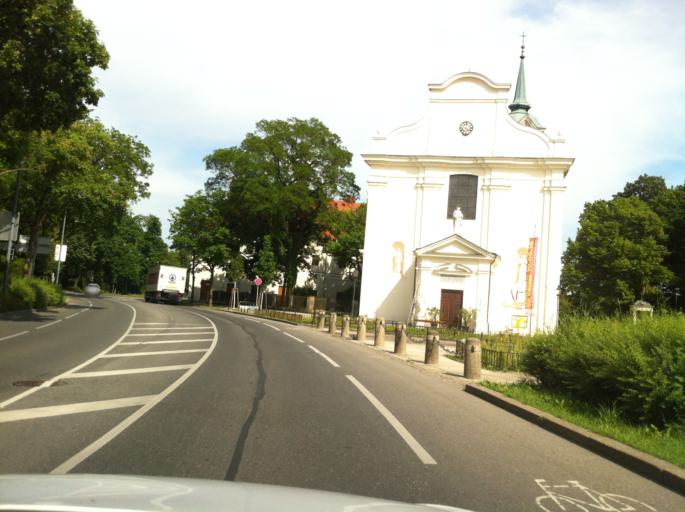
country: AT
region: Lower Austria
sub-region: Politischer Bezirk Wien-Umgebung
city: Purkersdorf
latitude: 48.2073
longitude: 16.2269
